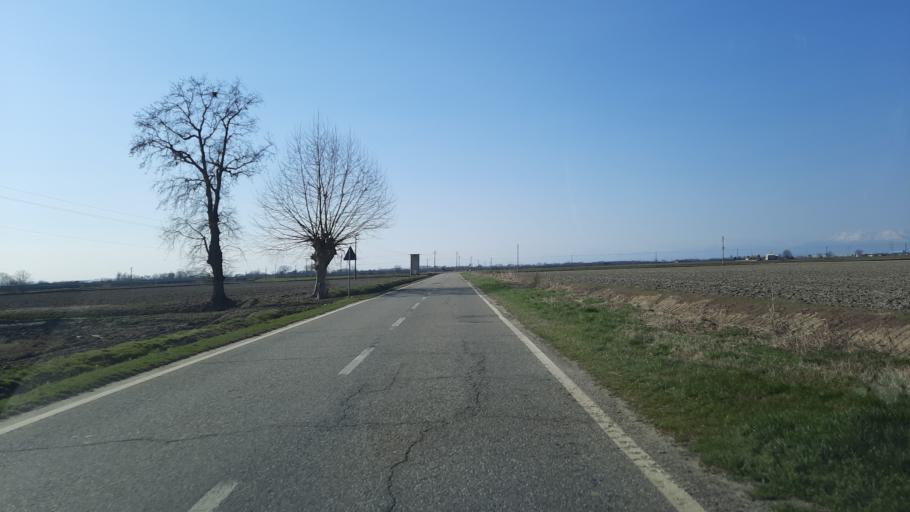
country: IT
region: Piedmont
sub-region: Provincia di Vercelli
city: Stroppiana
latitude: 45.2628
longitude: 8.4467
